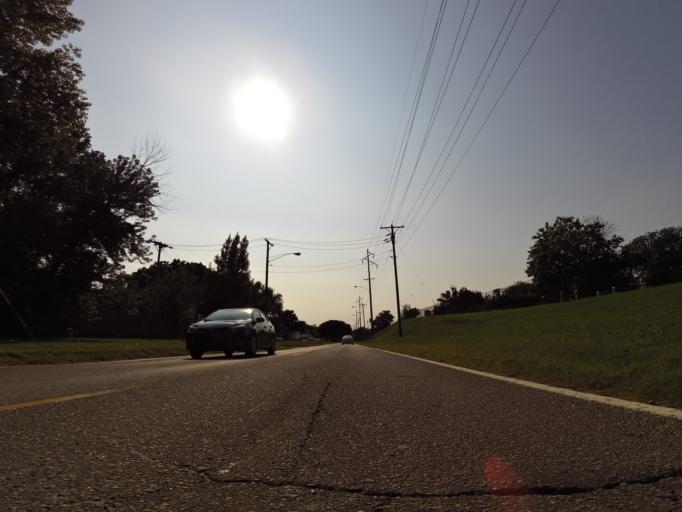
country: US
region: Kansas
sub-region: Sedgwick County
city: Wichita
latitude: 37.7015
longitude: -97.3017
